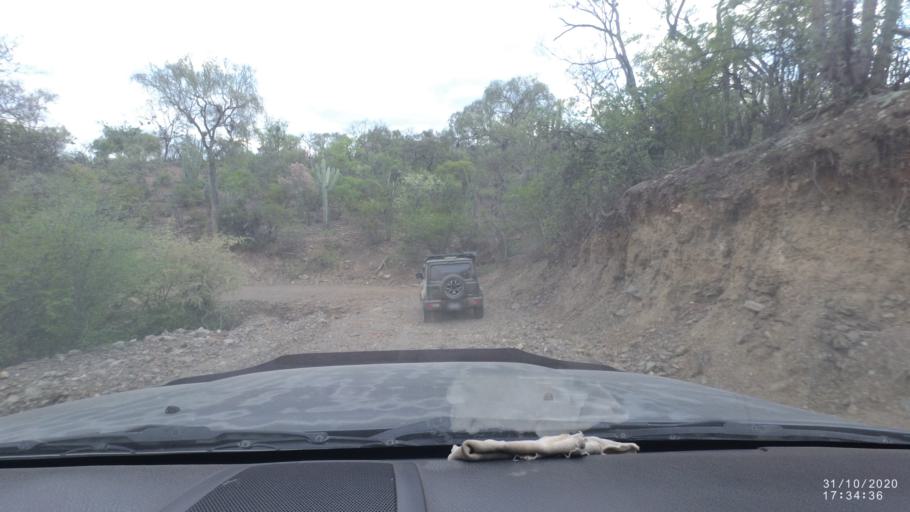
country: BO
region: Chuquisaca
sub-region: Provincia Zudanez
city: Mojocoya
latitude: -18.6013
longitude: -64.5487
